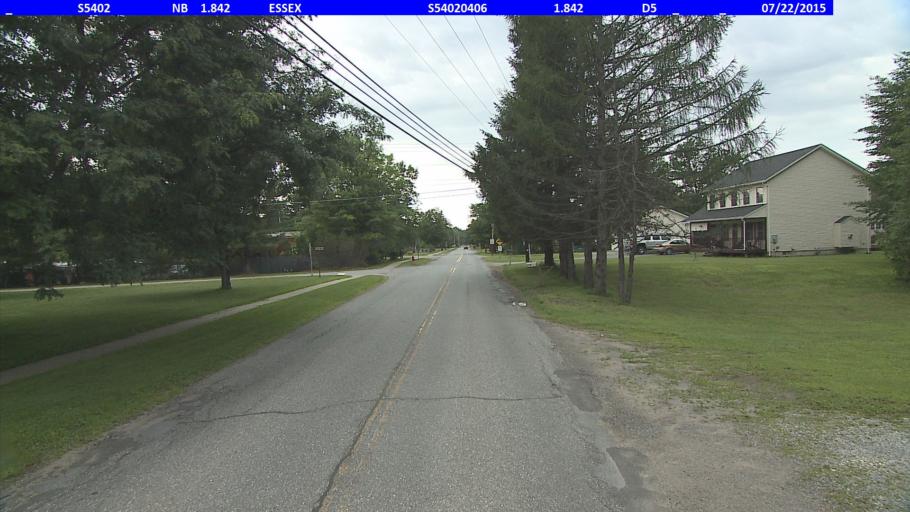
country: US
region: Vermont
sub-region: Chittenden County
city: Jericho
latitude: 44.5042
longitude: -73.0517
